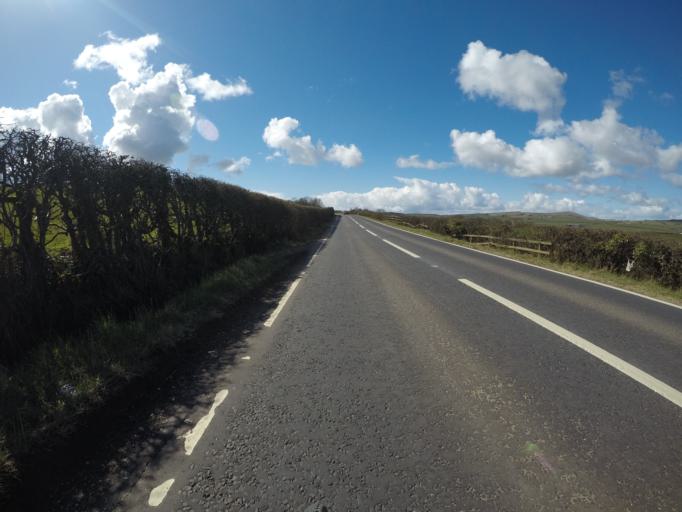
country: GB
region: Scotland
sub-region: North Ayrshire
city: Dalry
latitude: 55.6965
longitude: -4.7343
